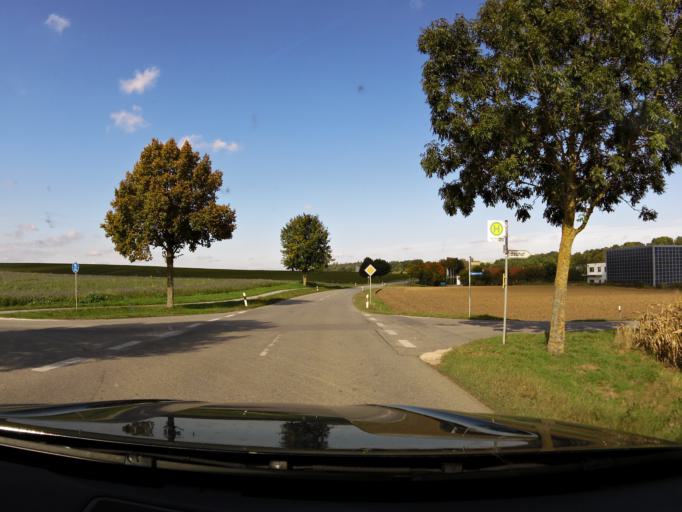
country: DE
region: Bavaria
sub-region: Lower Bavaria
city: Tiefenbach
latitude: 48.4921
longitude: 12.1011
